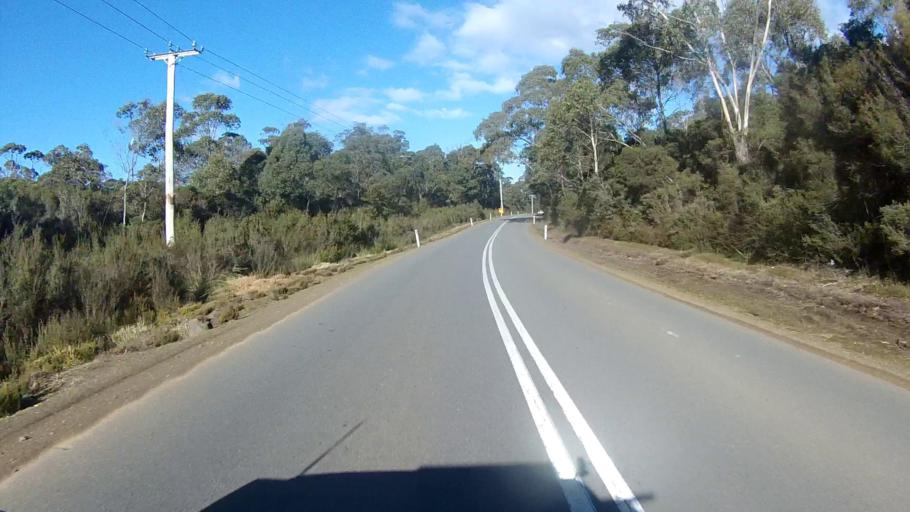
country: AU
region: Tasmania
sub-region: Clarence
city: Sandford
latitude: -43.0897
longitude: 147.8700
